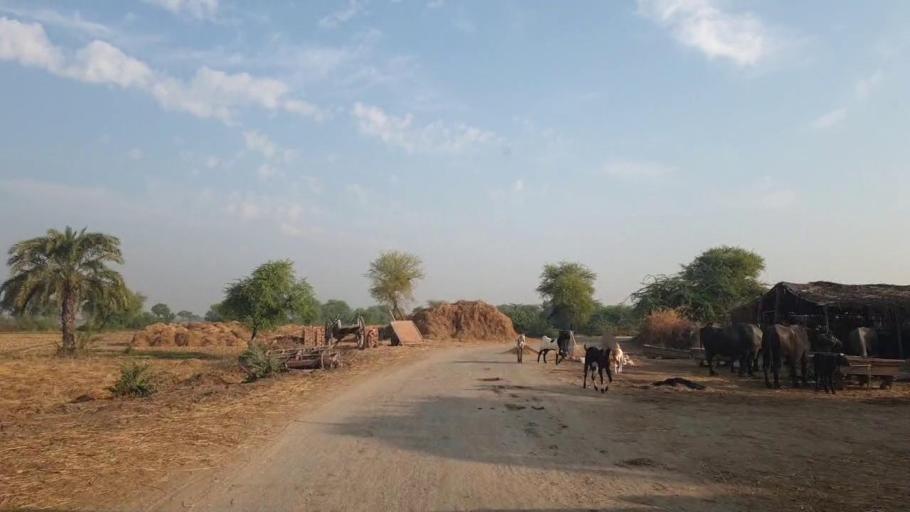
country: PK
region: Sindh
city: Tando Bago
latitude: 24.7913
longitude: 68.9613
